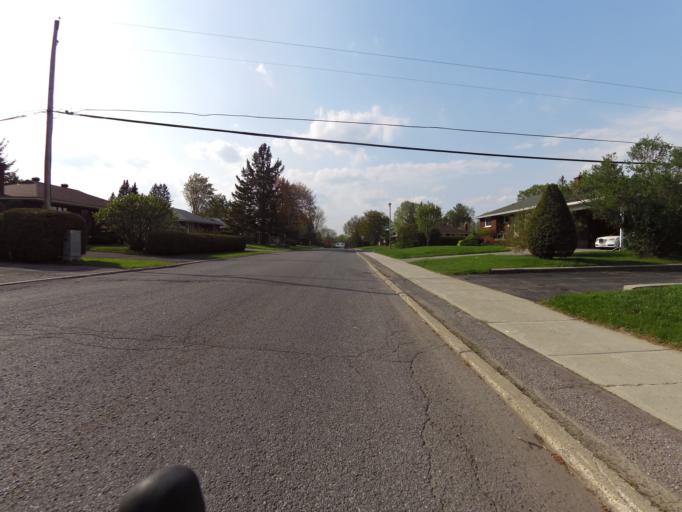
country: CA
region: Ontario
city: Bells Corners
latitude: 45.3273
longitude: -75.7616
